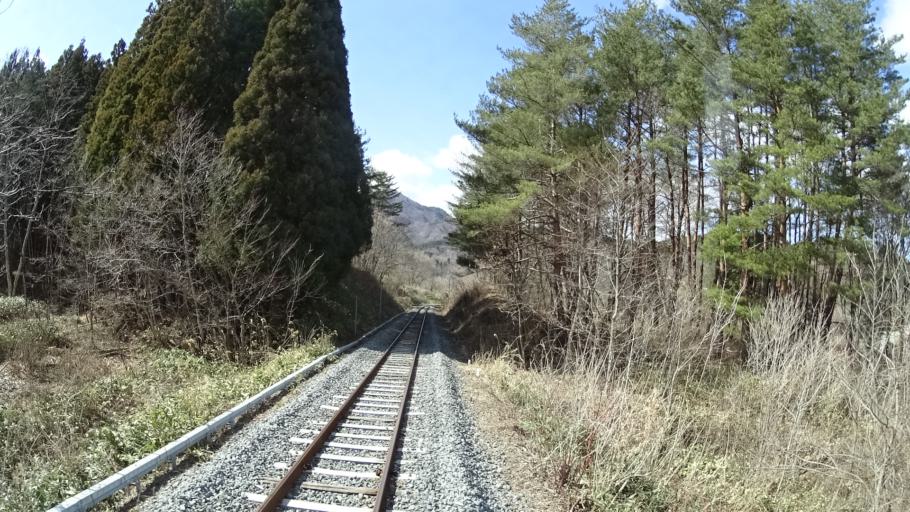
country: JP
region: Iwate
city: Yamada
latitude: 39.5089
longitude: 141.9171
